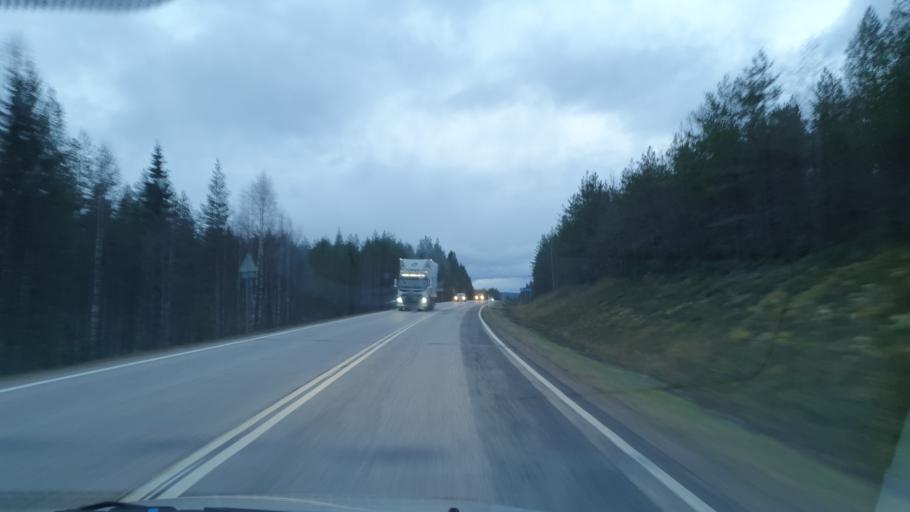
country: FI
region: Kainuu
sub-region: Kehys-Kainuu
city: Hyrynsalmi
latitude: 64.5944
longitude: 28.4352
